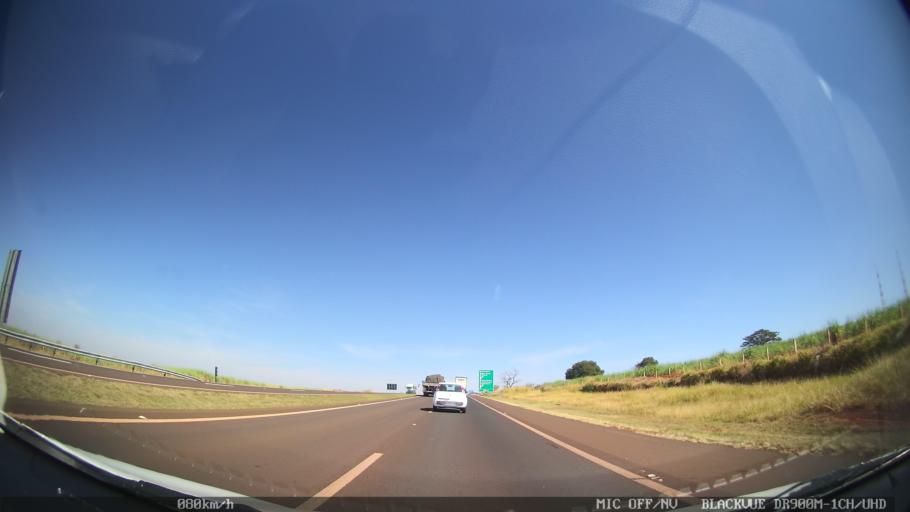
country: BR
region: Sao Paulo
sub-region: Ribeirao Preto
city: Ribeirao Preto
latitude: -21.1588
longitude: -47.8953
